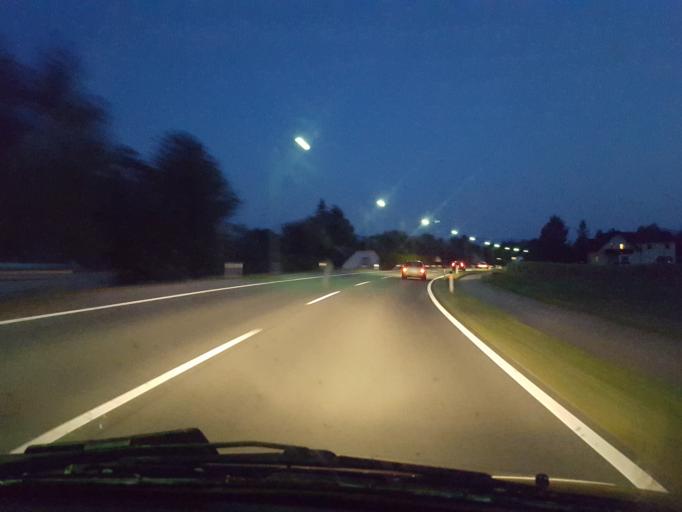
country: AT
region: Lower Austria
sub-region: Politischer Bezirk Scheibbs
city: Wieselburg
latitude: 48.1079
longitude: 15.1385
